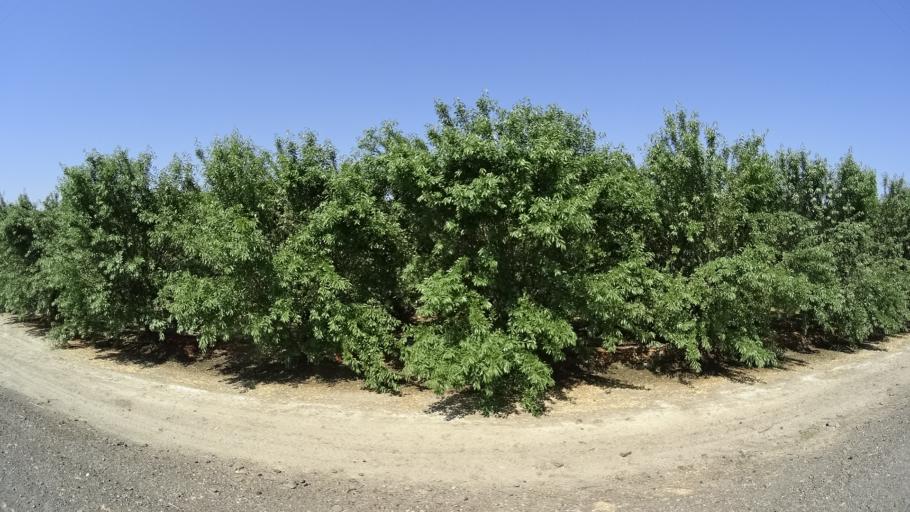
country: US
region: California
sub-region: Fresno County
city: Kingsburg
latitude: 36.4400
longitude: -119.5286
